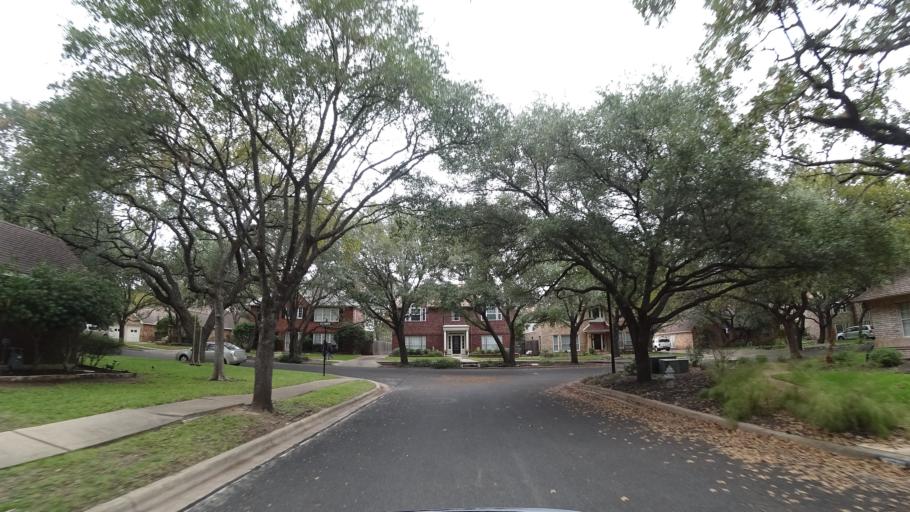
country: US
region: Texas
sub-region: Travis County
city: Shady Hollow
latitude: 30.1940
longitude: -97.8907
